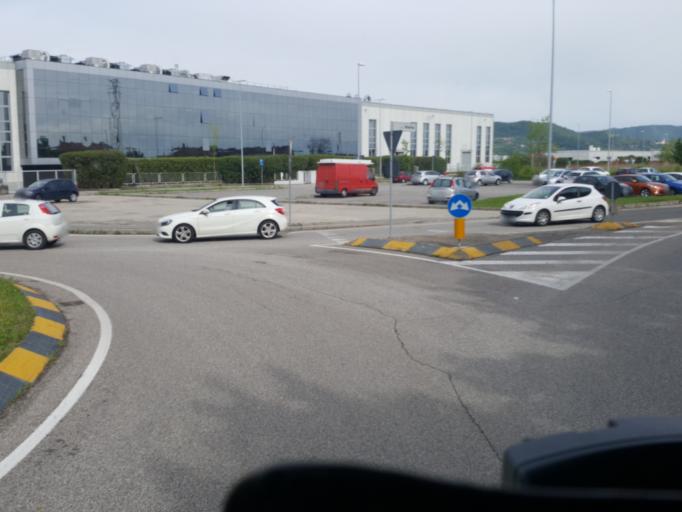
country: IT
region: Veneto
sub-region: Provincia di Vicenza
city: Montecchio Maggiore-Alte Ceccato
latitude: 45.4936
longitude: 11.4070
